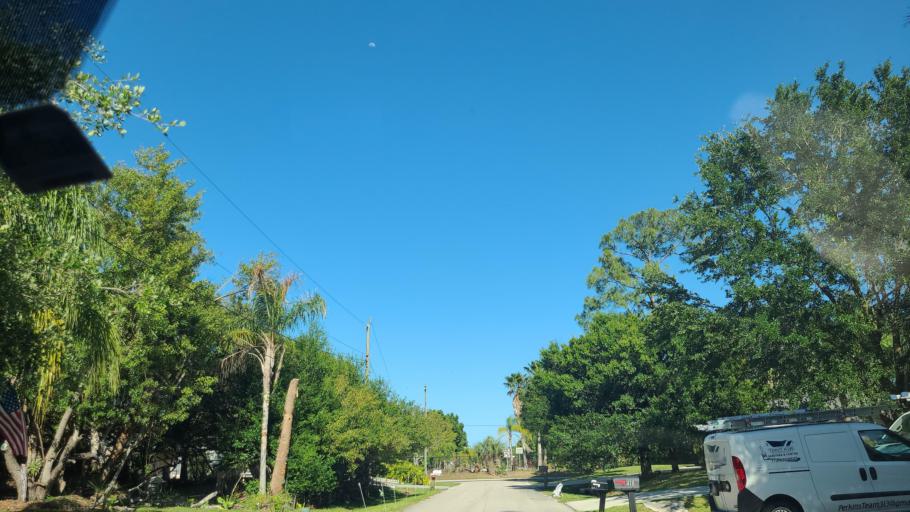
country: US
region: Florida
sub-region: Indian River County
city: Sebastian
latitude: 27.7561
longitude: -80.4793
